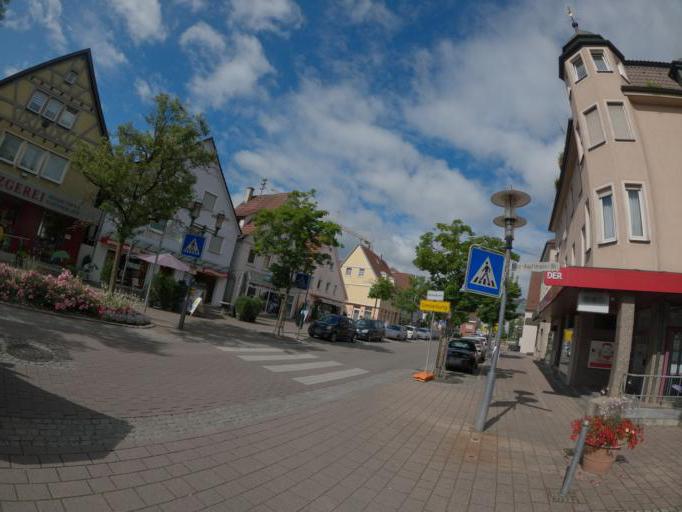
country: DE
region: Baden-Wuerttemberg
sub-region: Regierungsbezirk Stuttgart
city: Ebersbach an der Fils
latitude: 48.7142
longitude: 9.5245
